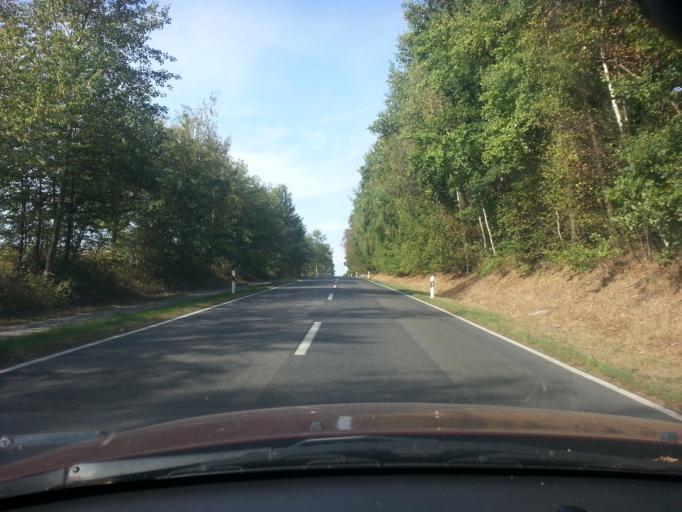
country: DE
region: Saxony
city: Goerlitz
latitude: 51.1200
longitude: 14.9606
